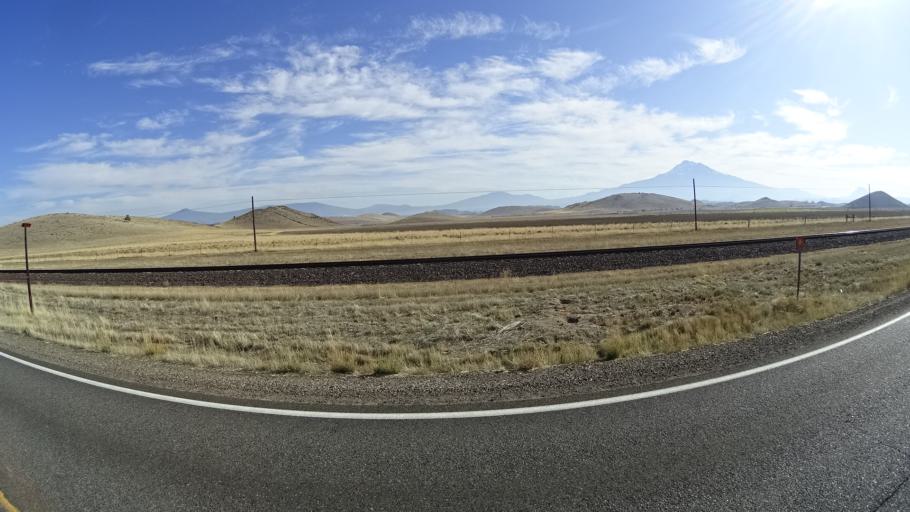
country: US
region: California
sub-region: Siskiyou County
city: Montague
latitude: 41.5510
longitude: -122.5262
